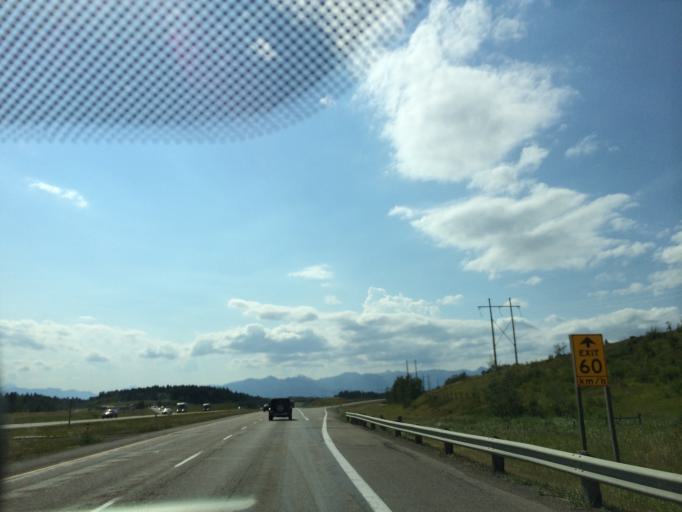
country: CA
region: Alberta
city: Cochrane
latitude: 51.1487
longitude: -114.8344
